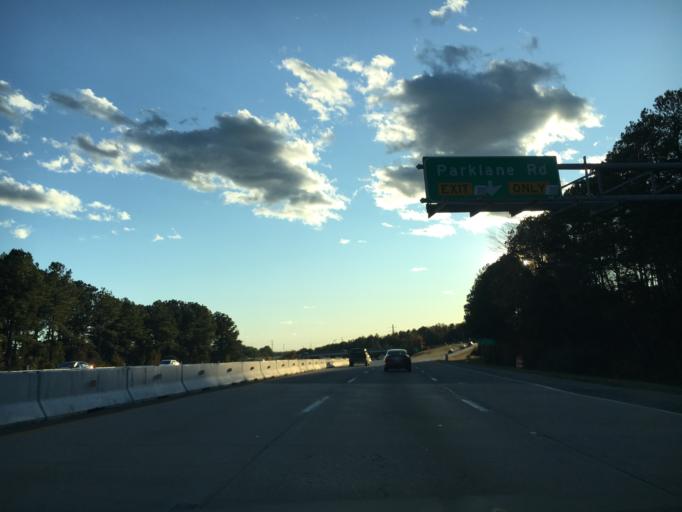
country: US
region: South Carolina
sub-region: Richland County
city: Dentsville
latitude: 34.0912
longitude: -80.9567
